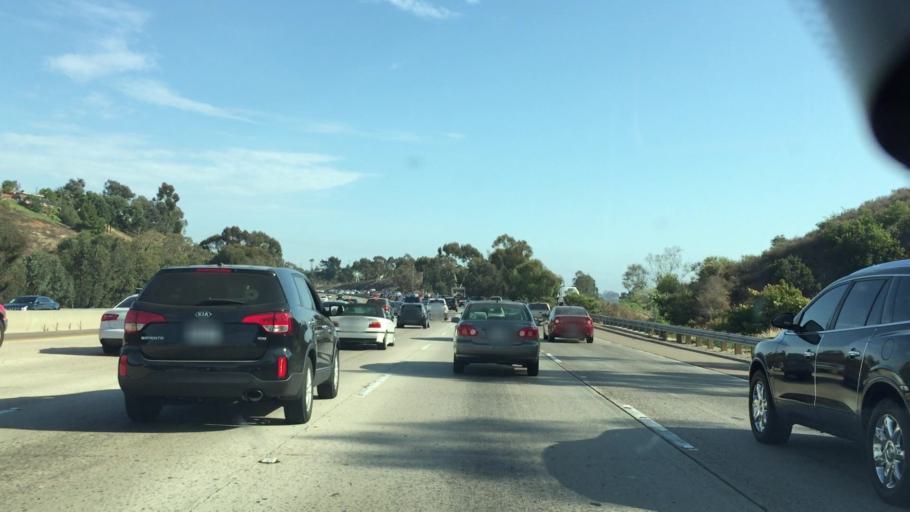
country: US
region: California
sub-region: San Diego County
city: San Diego
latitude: 32.7951
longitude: -117.1498
